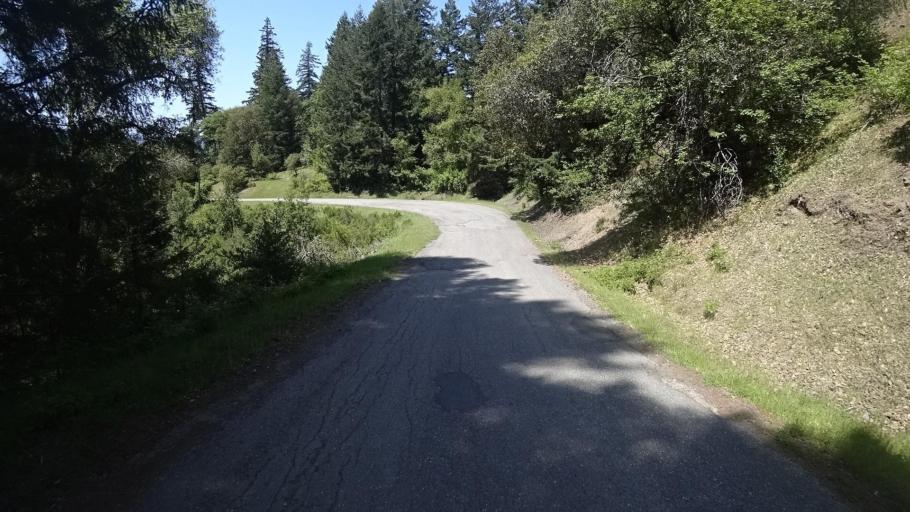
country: US
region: California
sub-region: Humboldt County
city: Redway
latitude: 40.1944
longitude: -123.5596
